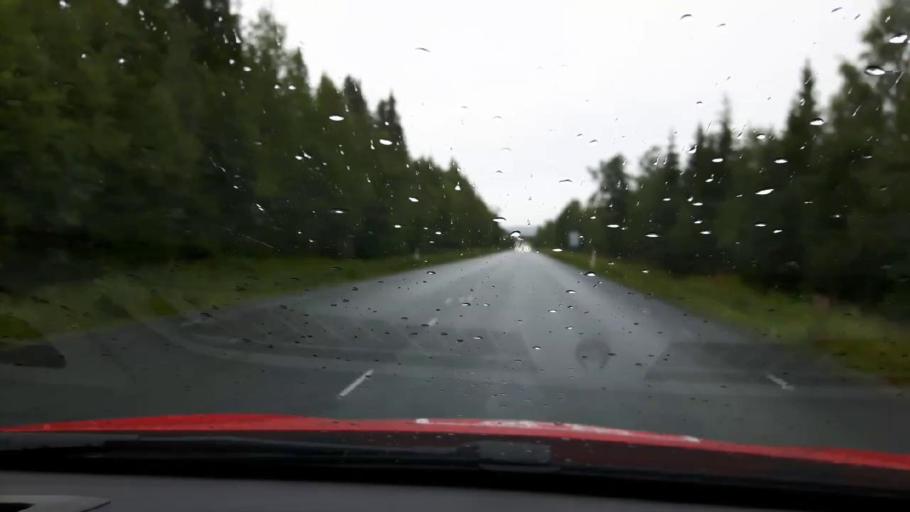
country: SE
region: Jaemtland
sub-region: Are Kommun
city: Are
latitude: 63.3978
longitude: 12.8501
